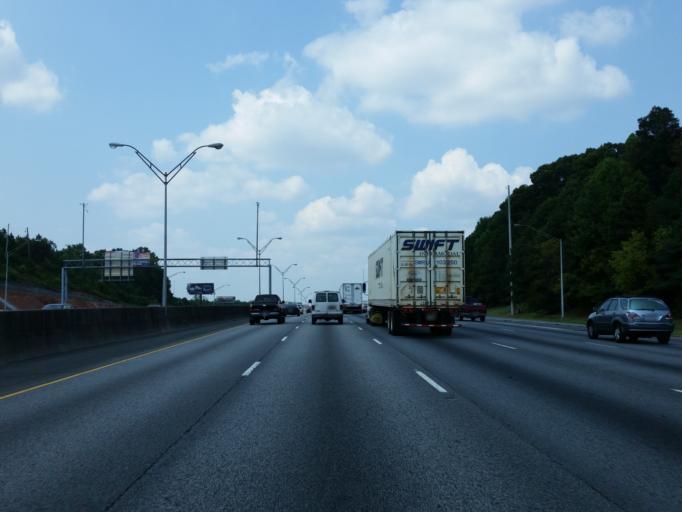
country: US
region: Georgia
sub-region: Cobb County
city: Marietta
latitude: 33.9637
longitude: -84.5217
